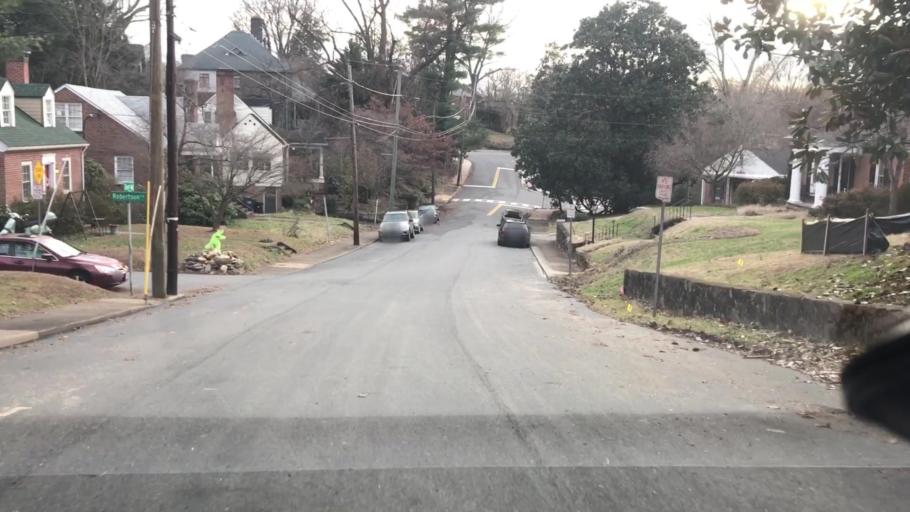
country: US
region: Virginia
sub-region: City of Charlottesville
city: Charlottesville
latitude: 38.0378
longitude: -78.4766
